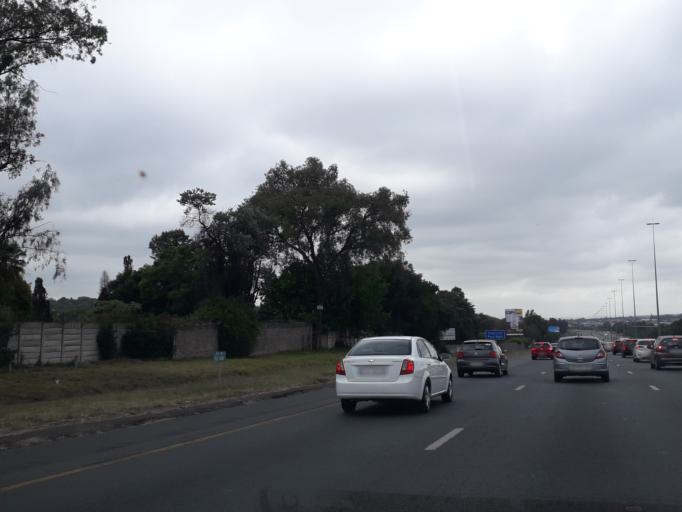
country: ZA
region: Gauteng
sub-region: City of Johannesburg Metropolitan Municipality
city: Roodepoort
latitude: -26.1050
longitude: 27.9610
